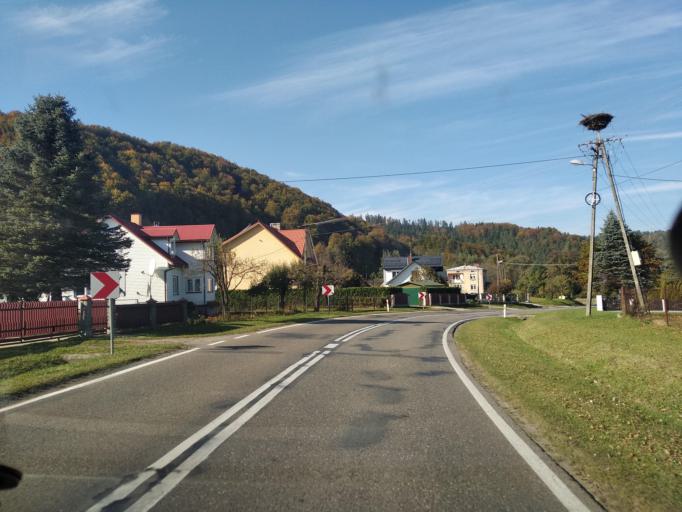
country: PL
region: Subcarpathian Voivodeship
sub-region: Powiat leski
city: Baligrod
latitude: 49.3938
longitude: 22.2813
